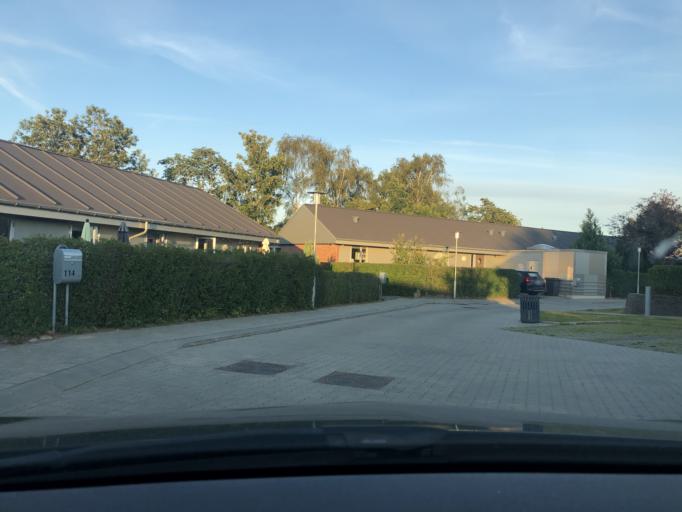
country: DK
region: South Denmark
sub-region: Vejle Kommune
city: Vejle
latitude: 55.6800
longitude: 9.5349
